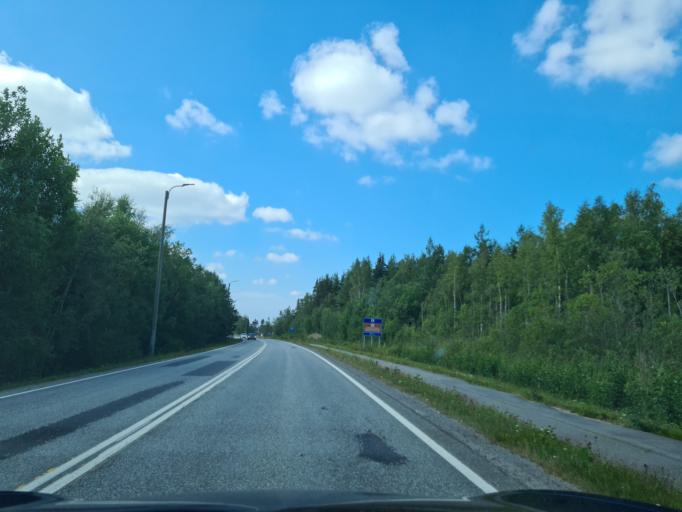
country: FI
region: Ostrobothnia
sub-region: Vaasa
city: Replot
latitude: 63.2038
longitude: 21.5250
